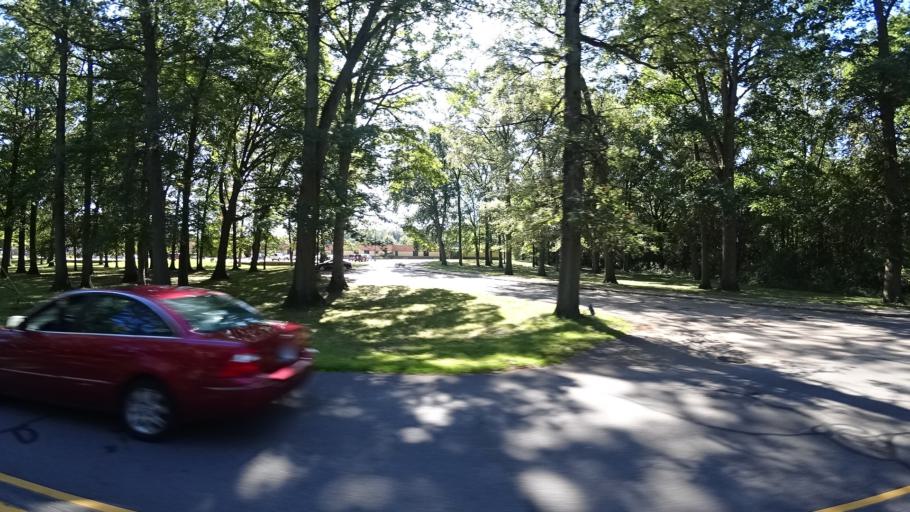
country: US
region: Indiana
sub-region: LaPorte County
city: Michigan City
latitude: 41.6876
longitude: -86.8862
